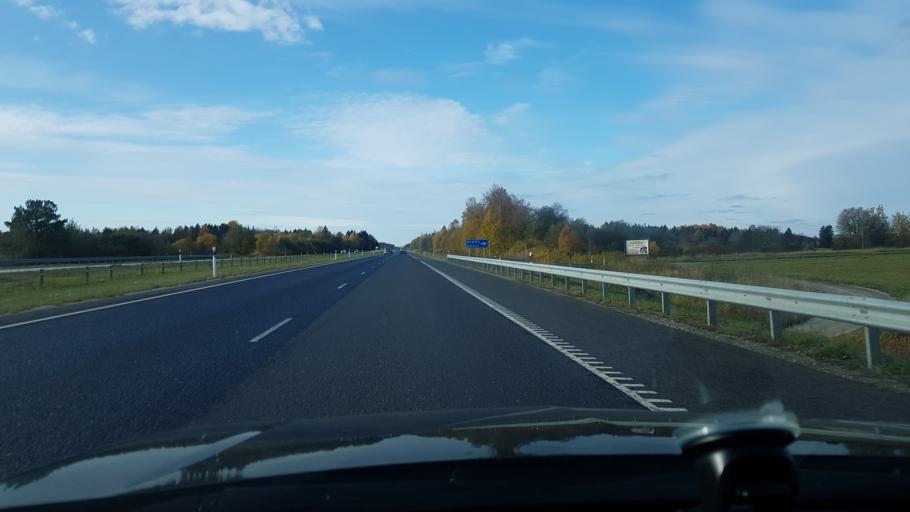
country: EE
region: Harju
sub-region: Anija vald
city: Kehra
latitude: 59.4414
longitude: 25.3053
